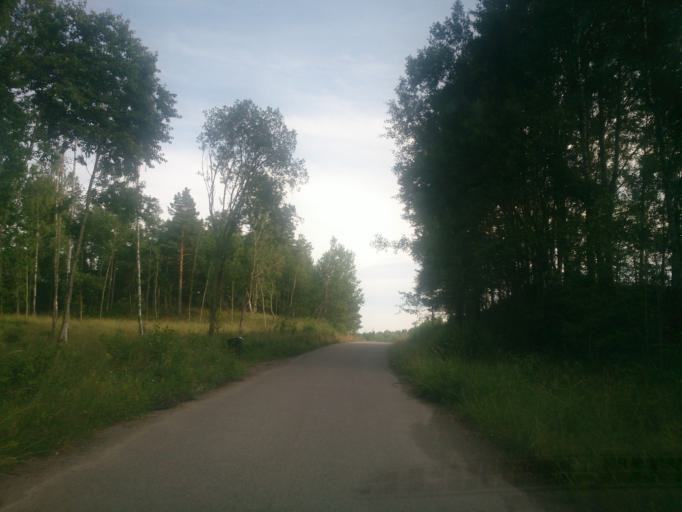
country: SE
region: OEstergoetland
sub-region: Atvidabergs Kommun
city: Atvidaberg
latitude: 58.2352
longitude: 15.9659
